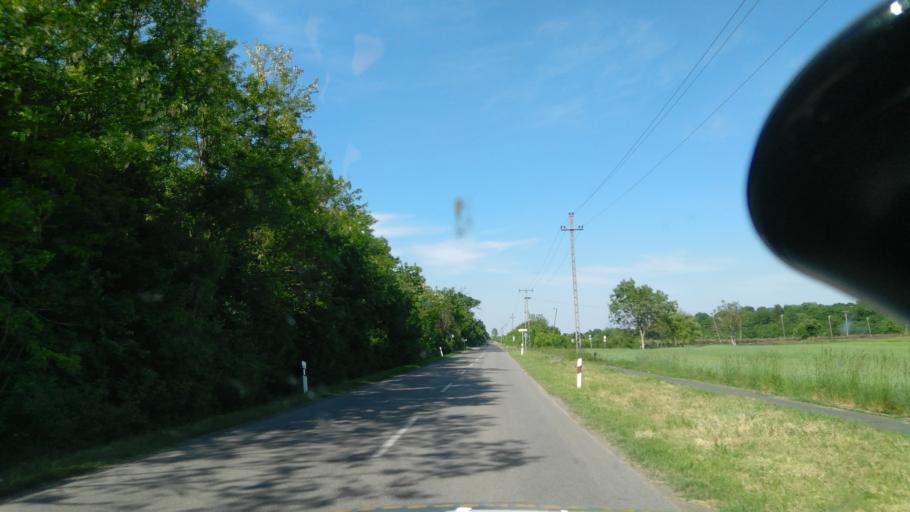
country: HU
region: Bekes
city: Gyula
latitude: 46.7034
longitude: 21.3144
